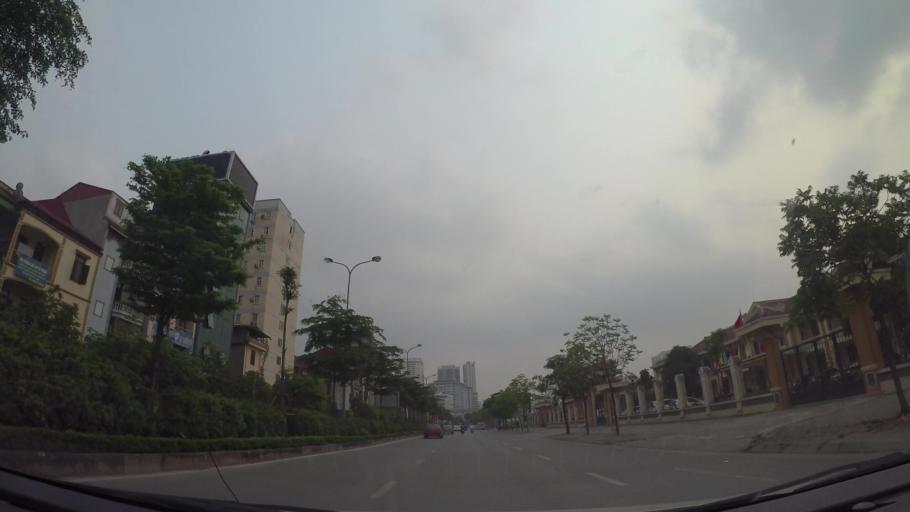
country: VN
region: Ha Noi
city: Cau Dien
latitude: 21.0411
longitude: 105.7730
